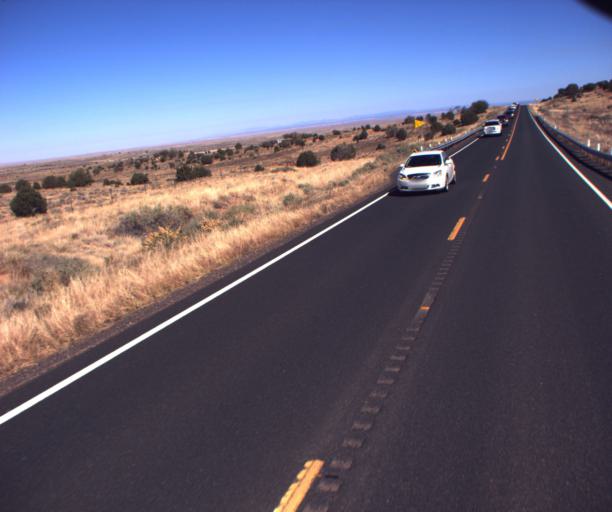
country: US
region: Arizona
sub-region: Apache County
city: Ganado
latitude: 35.7748
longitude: -109.7345
